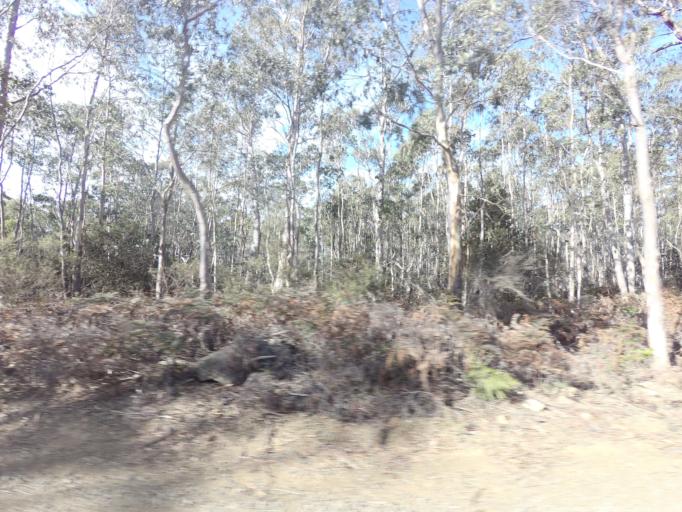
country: AU
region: Tasmania
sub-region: Sorell
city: Sorell
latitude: -42.4937
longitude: 147.4806
